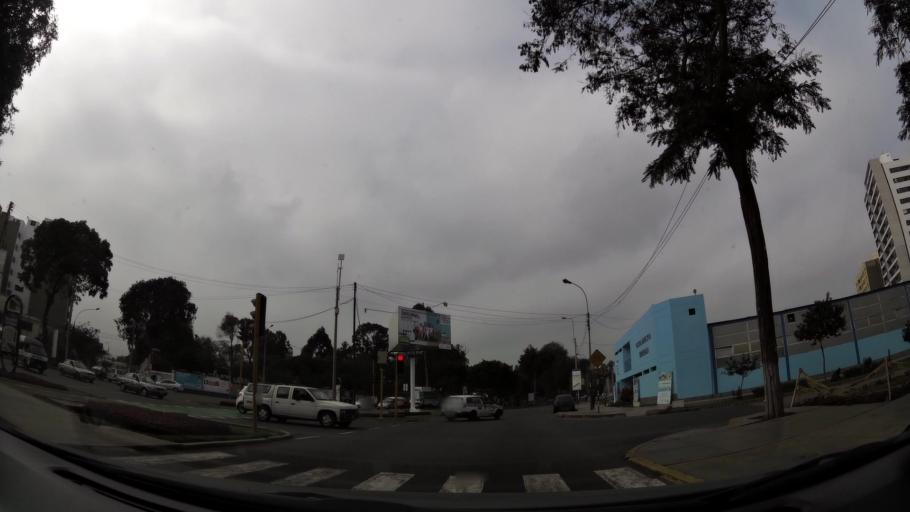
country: PE
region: Lima
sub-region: Lima
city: San Isidro
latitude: -12.0828
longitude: -77.0459
